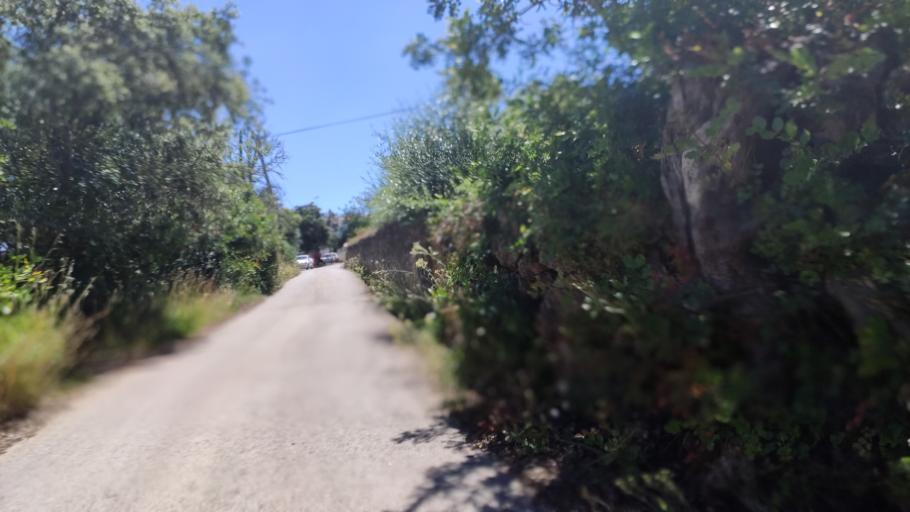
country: PT
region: Faro
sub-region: Sao Bras de Alportel
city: Sao Bras de Alportel
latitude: 37.1707
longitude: -7.9118
